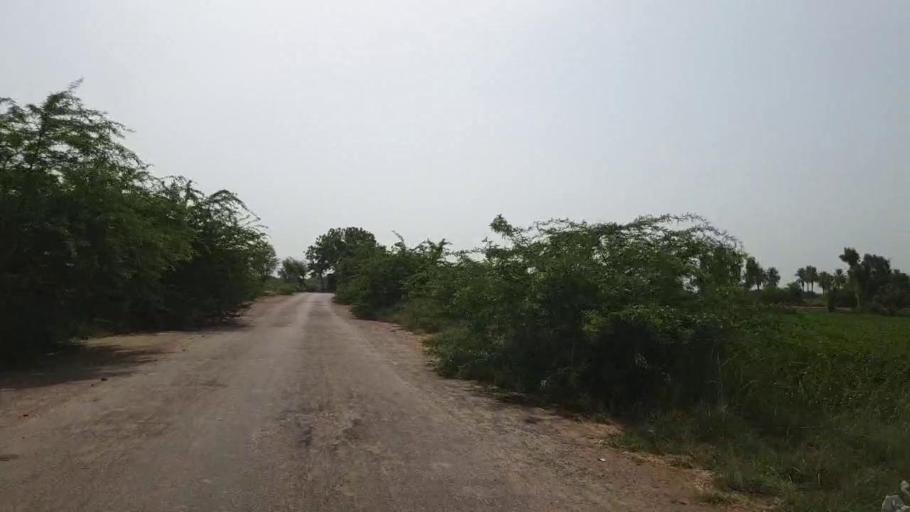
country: PK
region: Sindh
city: Bandhi
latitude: 26.5714
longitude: 68.3699
